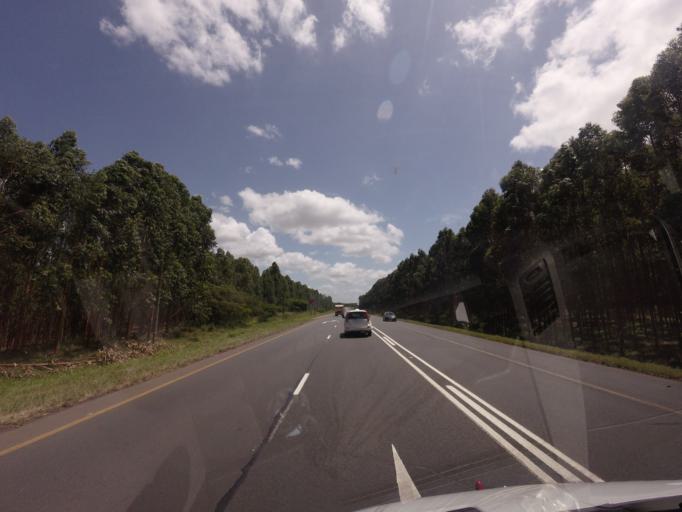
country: ZA
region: KwaZulu-Natal
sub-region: uThungulu District Municipality
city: KwaMbonambi
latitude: -28.5907
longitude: 32.0998
